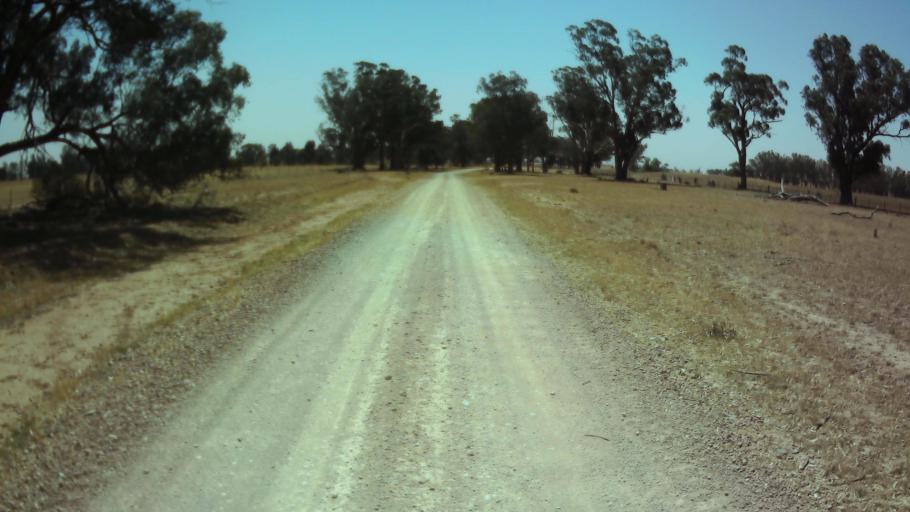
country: AU
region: New South Wales
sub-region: Weddin
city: Grenfell
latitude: -34.0177
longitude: 147.8989
